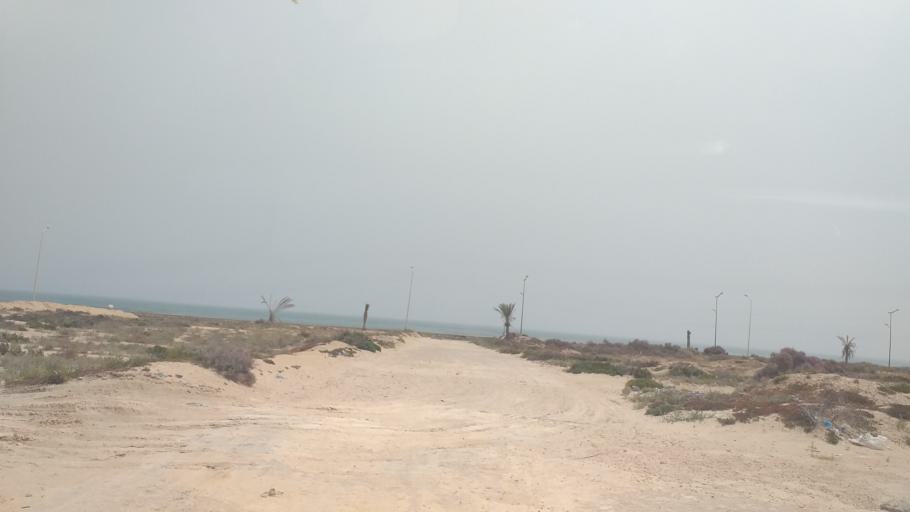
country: TN
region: Qabis
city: Gabes
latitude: 33.9565
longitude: 10.0679
